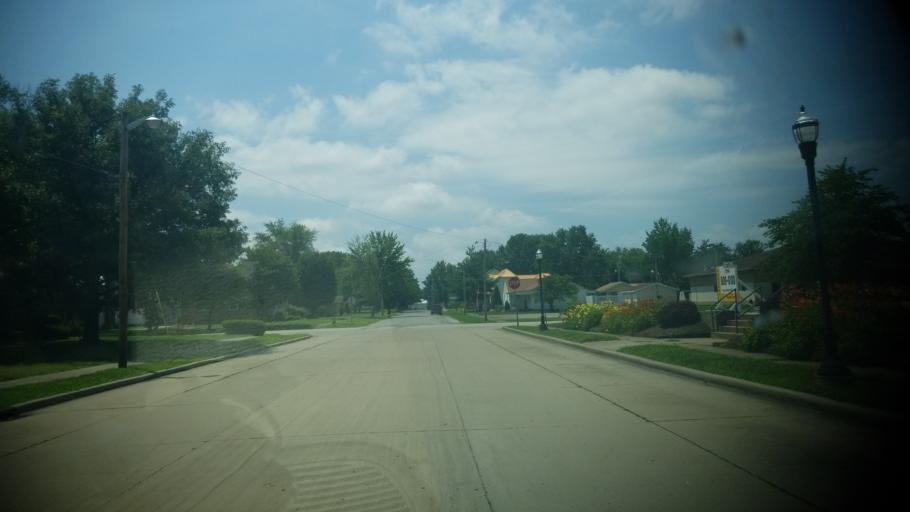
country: US
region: Illinois
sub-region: Wayne County
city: Fairfield
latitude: 38.3781
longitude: -88.3579
